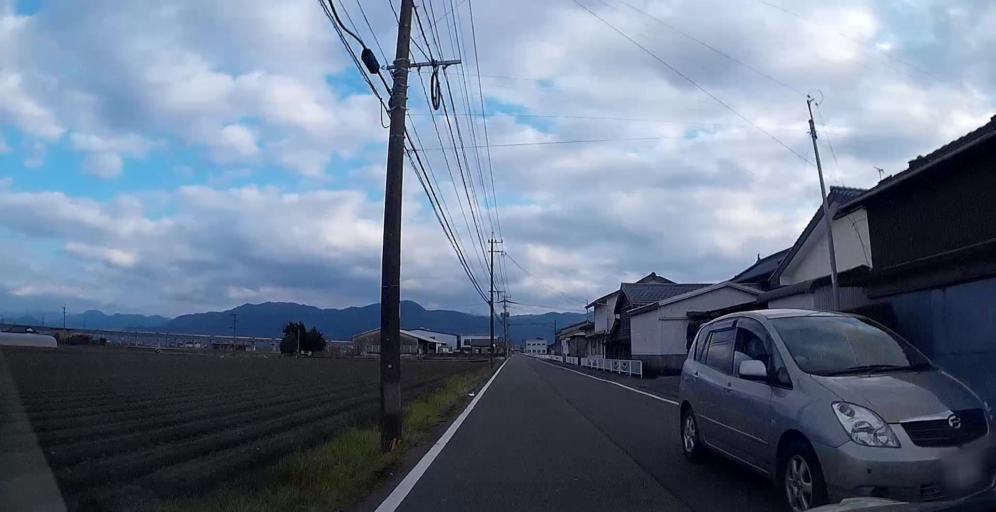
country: JP
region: Kumamoto
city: Yatsushiro
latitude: 32.5454
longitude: 130.6188
